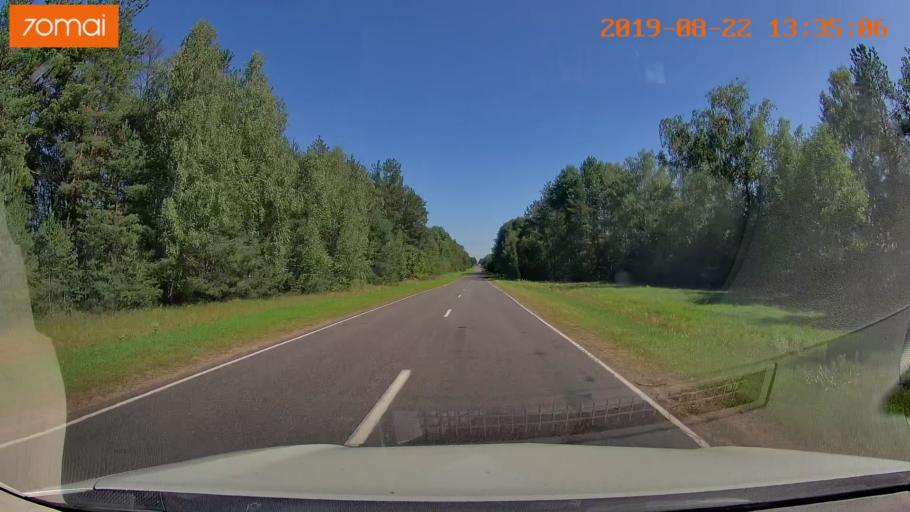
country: BY
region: Minsk
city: Staryya Darohi
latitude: 53.2142
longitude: 28.2591
